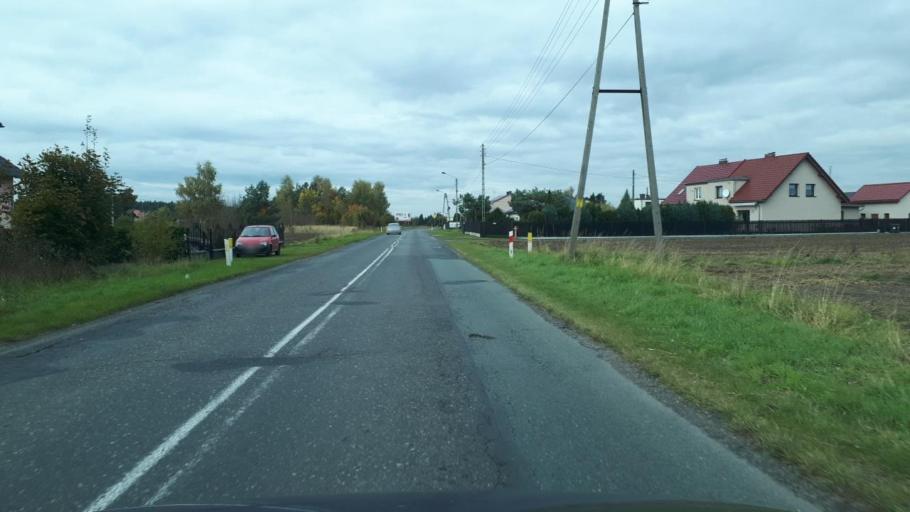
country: PL
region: Opole Voivodeship
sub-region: Powiat strzelecki
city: Zawadzkie
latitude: 50.5881
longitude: 18.5043
